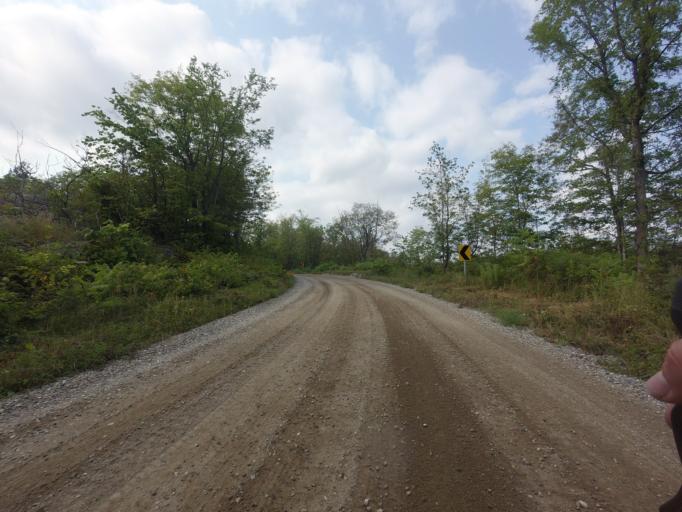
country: CA
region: Ontario
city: Perth
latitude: 44.8437
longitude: -76.7182
